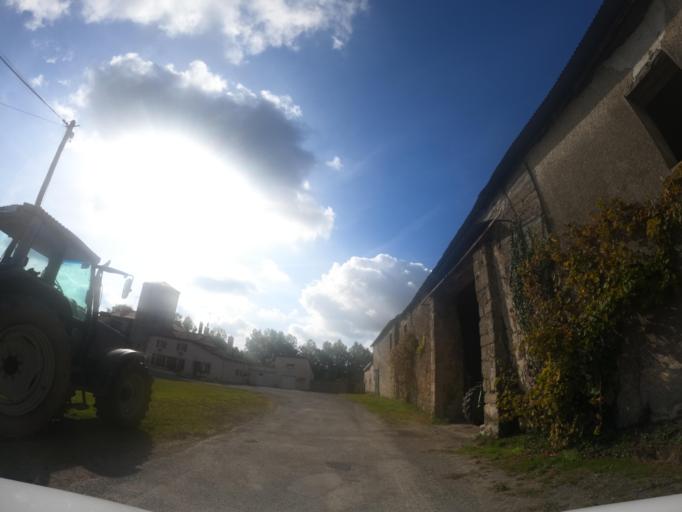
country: FR
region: Poitou-Charentes
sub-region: Departement des Deux-Sevres
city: Courlay
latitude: 46.7736
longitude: -0.6003
